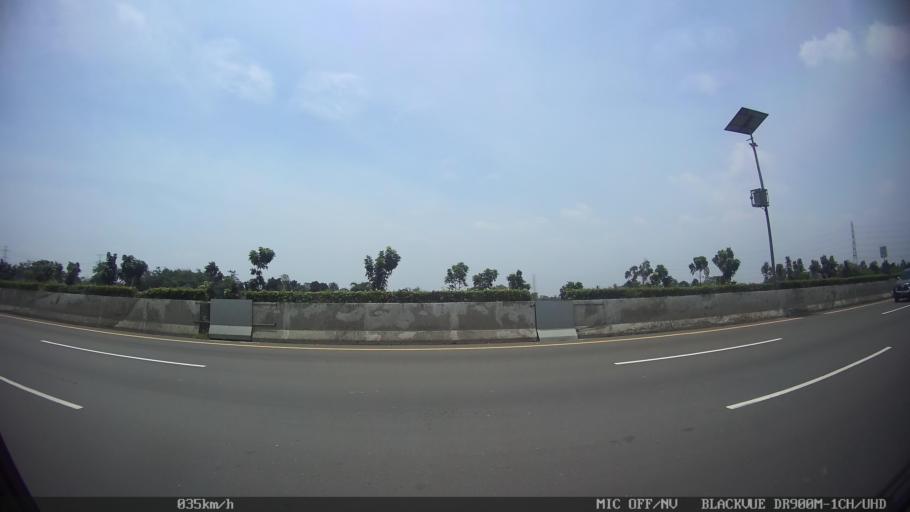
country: ID
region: West Java
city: Kresek
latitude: -6.1927
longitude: 106.4237
